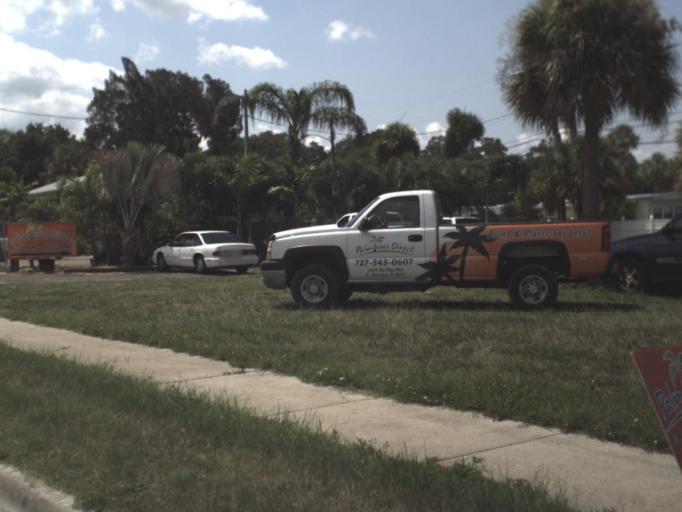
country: US
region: Florida
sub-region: Pinellas County
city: Bay Pines
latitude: 27.8119
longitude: -82.7585
